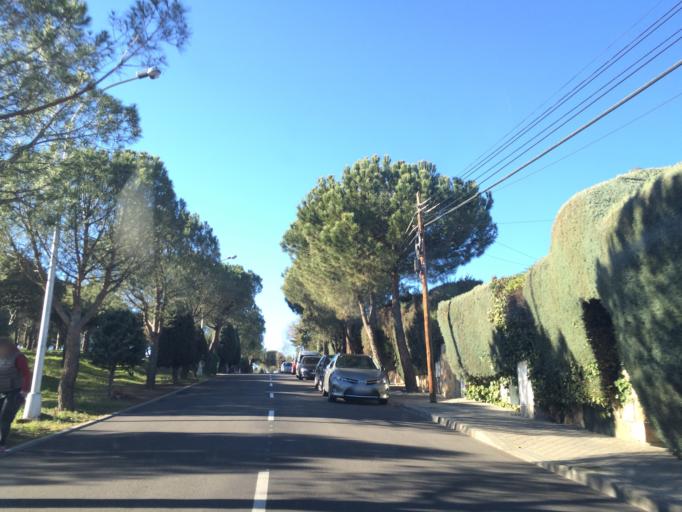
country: ES
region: Madrid
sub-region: Provincia de Madrid
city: Tres Cantos
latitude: 40.6092
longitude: -3.6862
